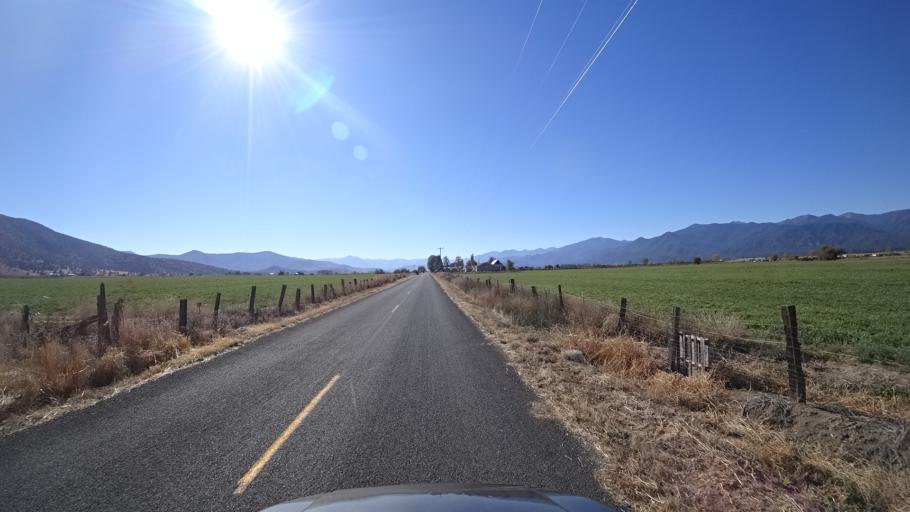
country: US
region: California
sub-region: Siskiyou County
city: Yreka
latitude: 41.5359
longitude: -122.8579
